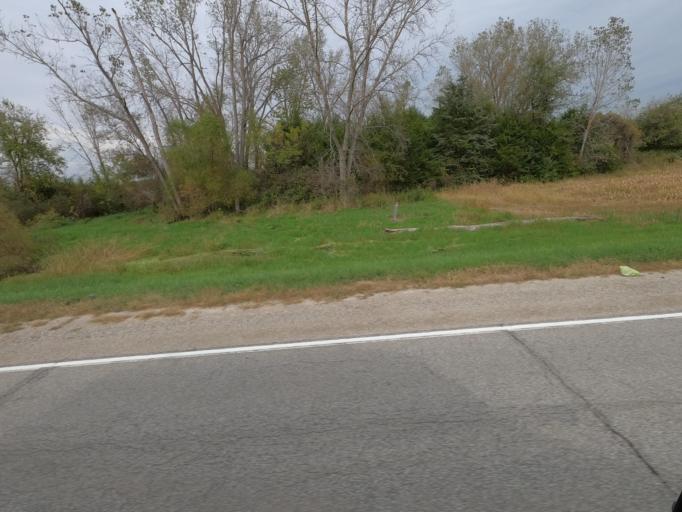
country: US
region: Iowa
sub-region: Van Buren County
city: Keosauqua
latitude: 40.8644
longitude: -92.1389
